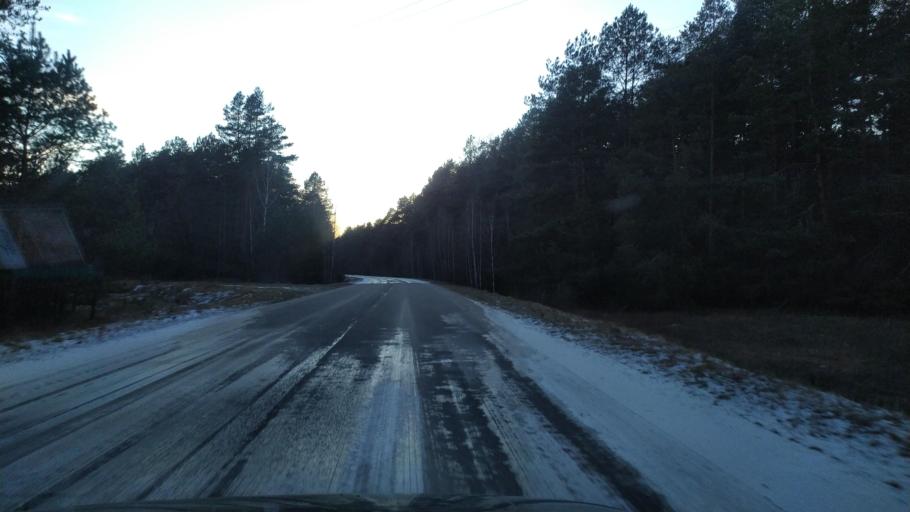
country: BY
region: Brest
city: Pruzhany
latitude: 52.5311
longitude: 24.1856
